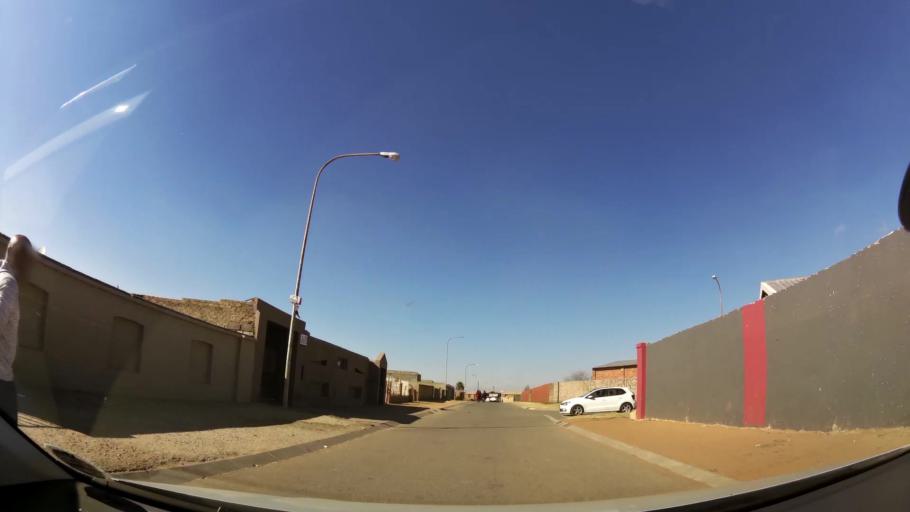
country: ZA
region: Gauteng
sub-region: City of Johannesburg Metropolitan Municipality
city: Roodepoort
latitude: -26.2127
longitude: 27.8991
